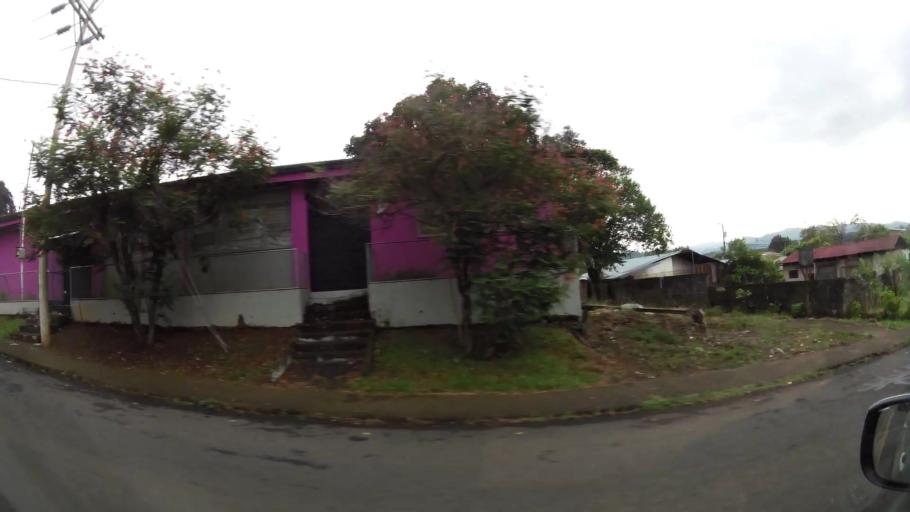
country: CR
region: Alajuela
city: Desamparados
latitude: 9.9347
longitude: -84.5214
